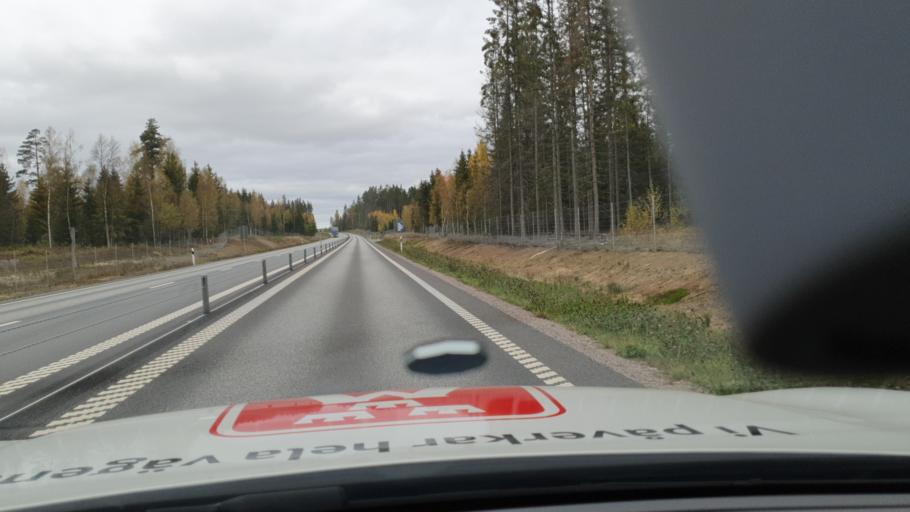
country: SE
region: OErebro
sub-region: Hallsbergs Kommun
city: Palsboda
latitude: 59.0324
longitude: 15.3594
